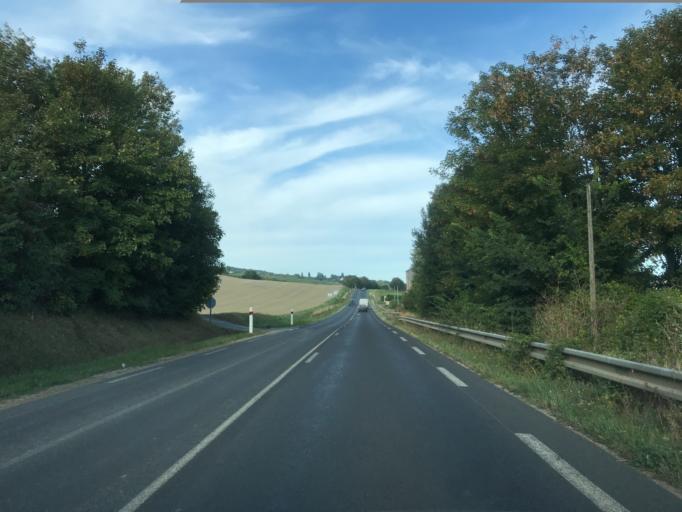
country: FR
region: Champagne-Ardenne
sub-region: Departement de la Marne
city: Mardeuil
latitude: 49.0530
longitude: 3.9096
